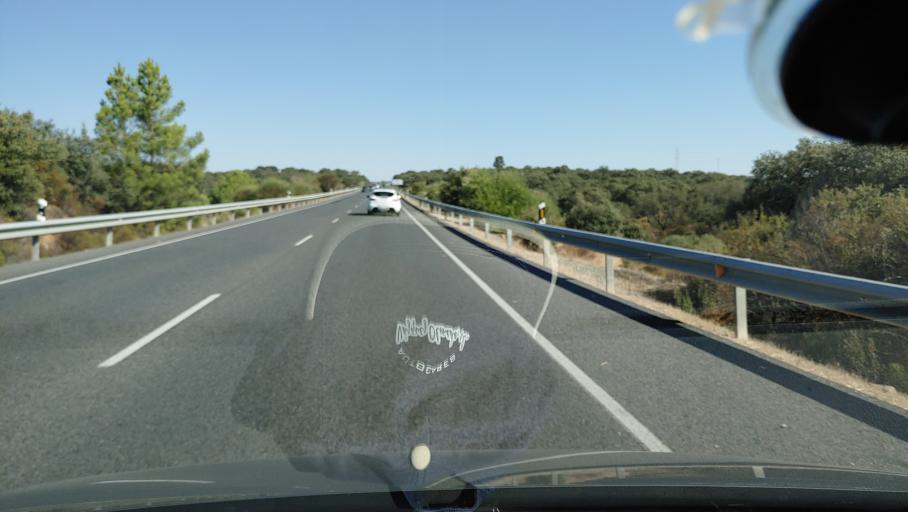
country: ES
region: Andalusia
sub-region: Province of Cordoba
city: Obejo
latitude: 38.0395
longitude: -4.8077
